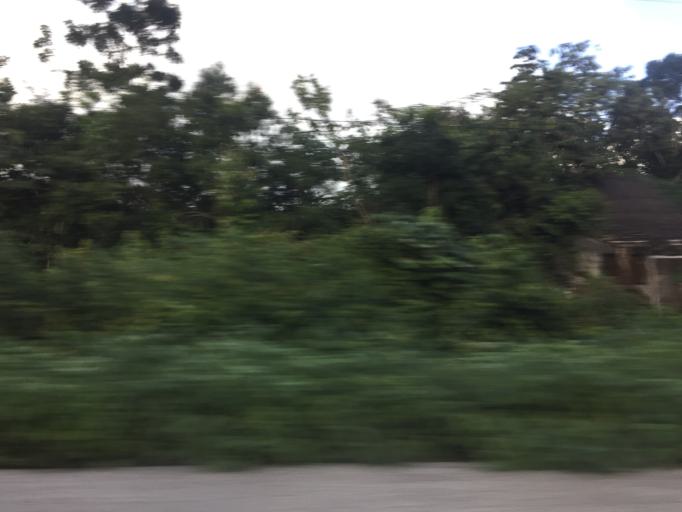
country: MX
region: Quintana Roo
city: Tulum
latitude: 20.2811
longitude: -87.4931
